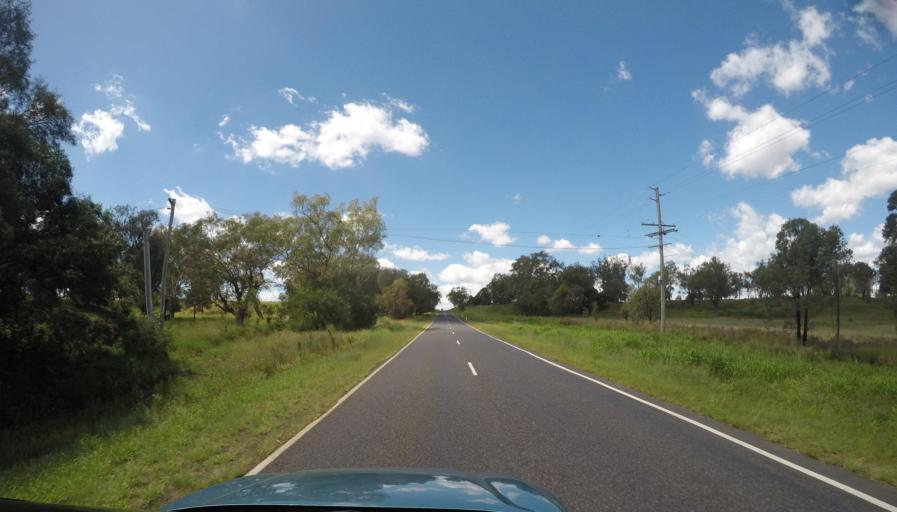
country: AU
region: Queensland
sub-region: Toowoomba
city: Oakey
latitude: -27.5435
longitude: 151.6659
